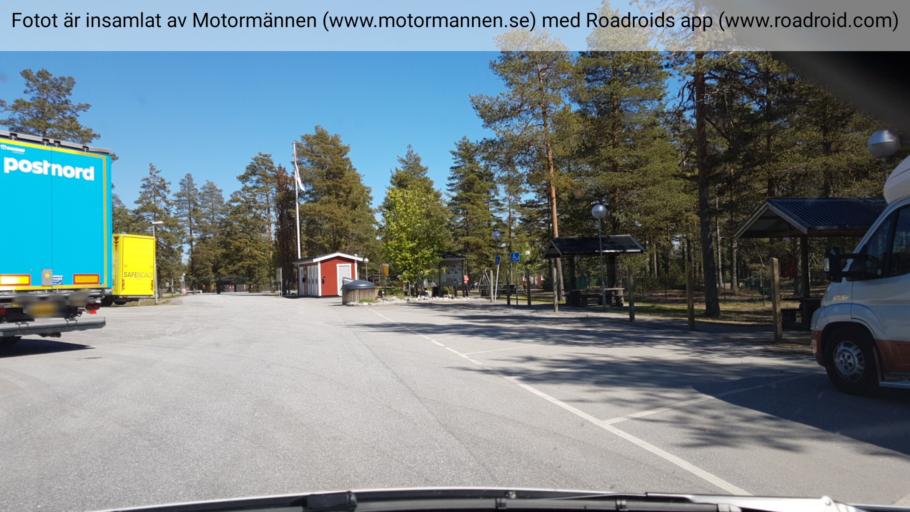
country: SE
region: Vaesternorrland
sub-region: OErnskoeldsviks Kommun
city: Husum
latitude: 63.3162
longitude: 19.0106
